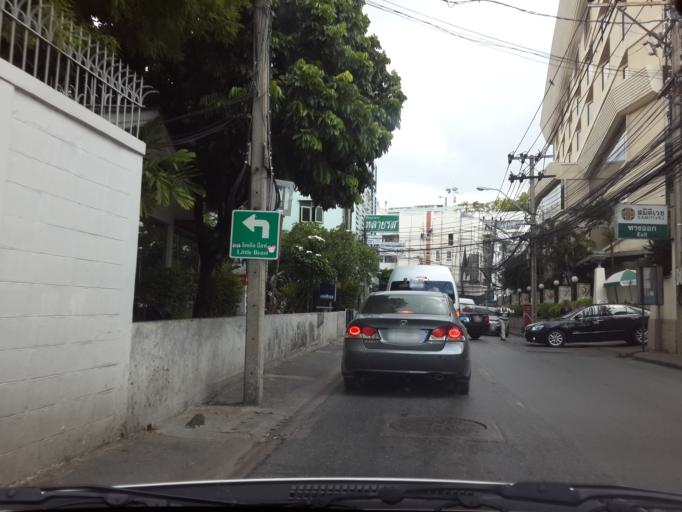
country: TH
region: Bangkok
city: Watthana
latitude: 13.7355
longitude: 100.5771
